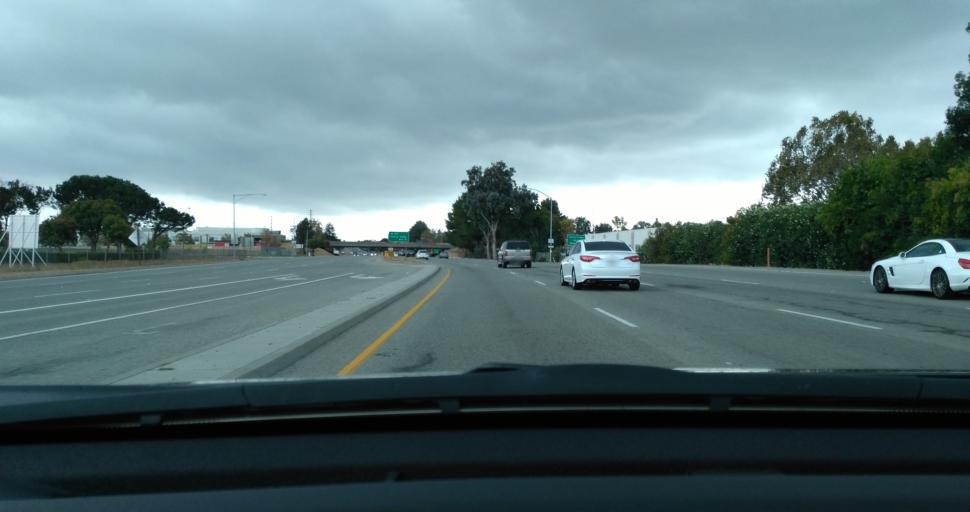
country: US
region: California
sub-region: Santa Clara County
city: Santa Clara
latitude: 37.3777
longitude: -121.9659
